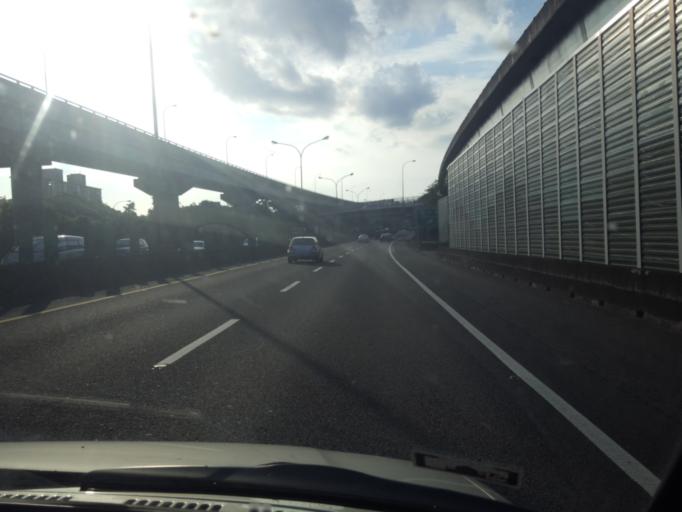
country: TW
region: Taipei
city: Taipei
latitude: 25.0638
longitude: 121.5979
